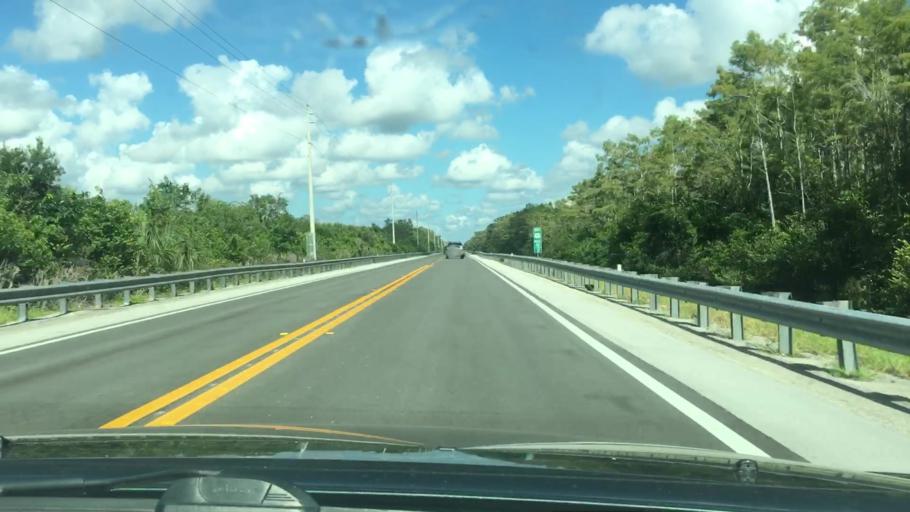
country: US
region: Florida
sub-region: Miami-Dade County
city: Kendall West
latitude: 25.7650
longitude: -80.8315
